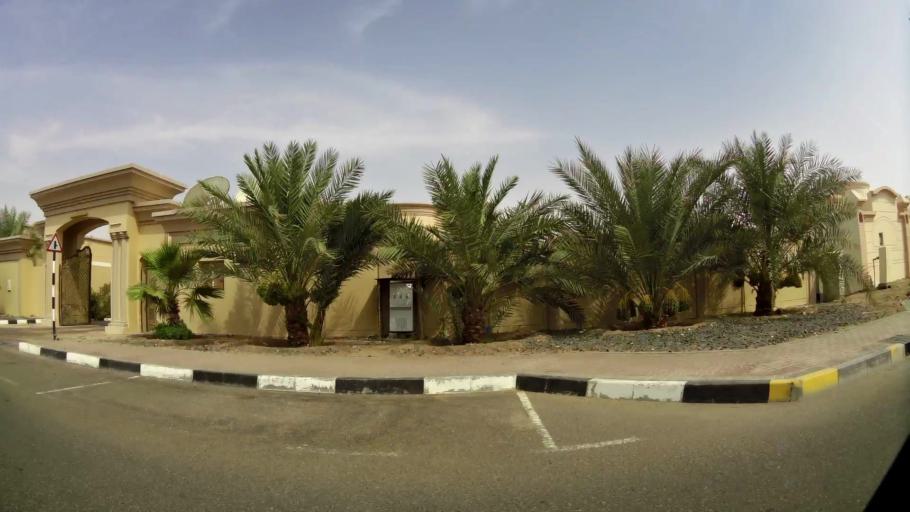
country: AE
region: Abu Dhabi
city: Al Ain
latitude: 24.1696
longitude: 55.6986
